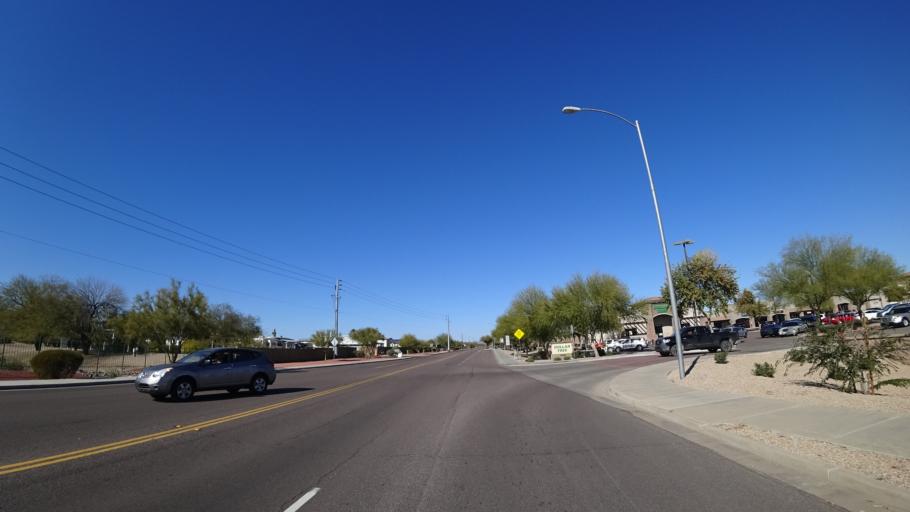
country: US
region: Arizona
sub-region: Maricopa County
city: Sun City West
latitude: 33.6395
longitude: -112.4267
